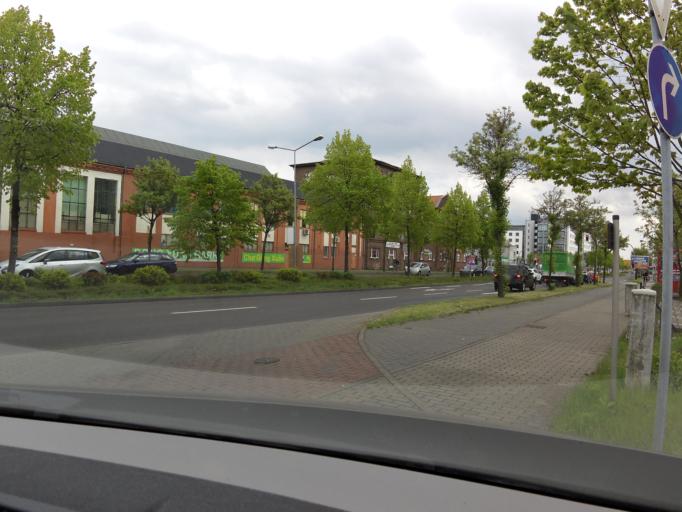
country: DE
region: Saxony
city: Leipzig
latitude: 51.3678
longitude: 12.3976
